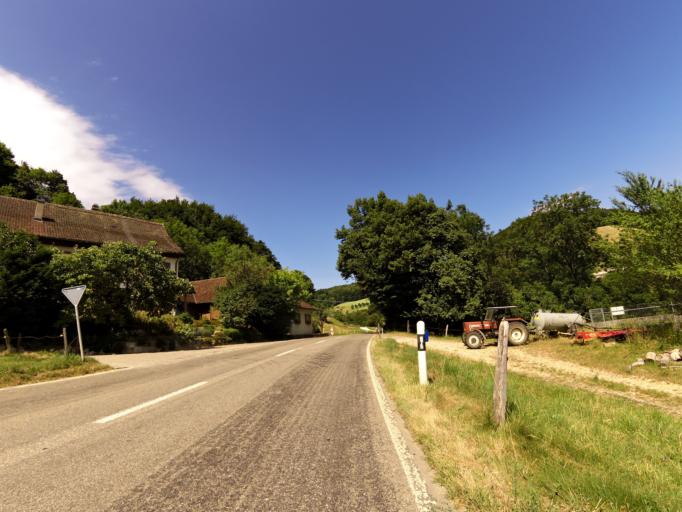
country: CH
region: Basel-Landschaft
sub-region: Bezirk Waldenburg
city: Langenbruck
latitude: 47.3414
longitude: 7.7681
